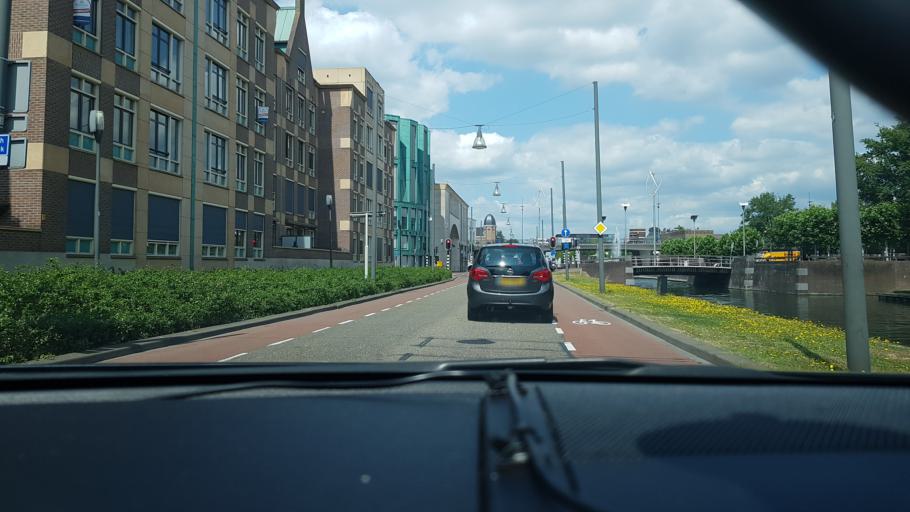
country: NL
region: North Brabant
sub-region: Gemeente Helmond
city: Helmond
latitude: 51.4768
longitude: 5.6515
